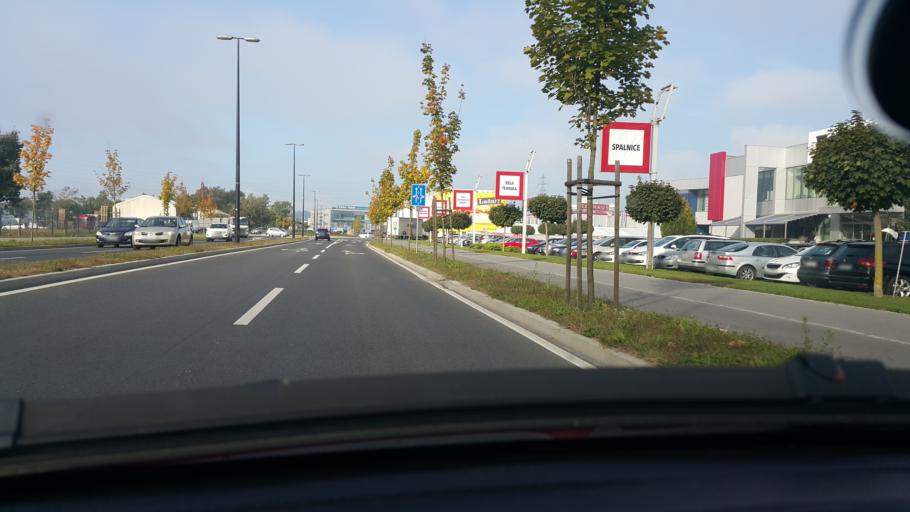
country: SI
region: Ljubljana
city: Ljubljana
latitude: 46.0612
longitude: 14.5437
